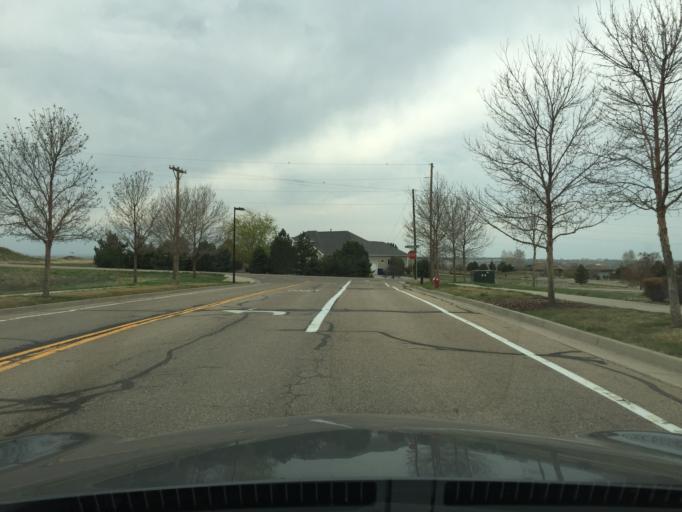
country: US
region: Colorado
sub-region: Boulder County
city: Erie
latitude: 40.0046
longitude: -105.0360
